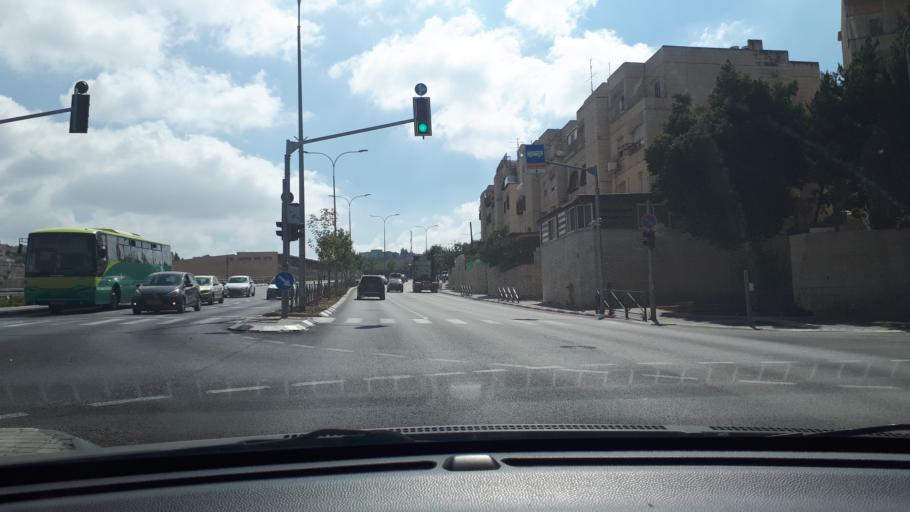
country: PS
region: West Bank
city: Hizma
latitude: 31.8260
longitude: 35.2426
